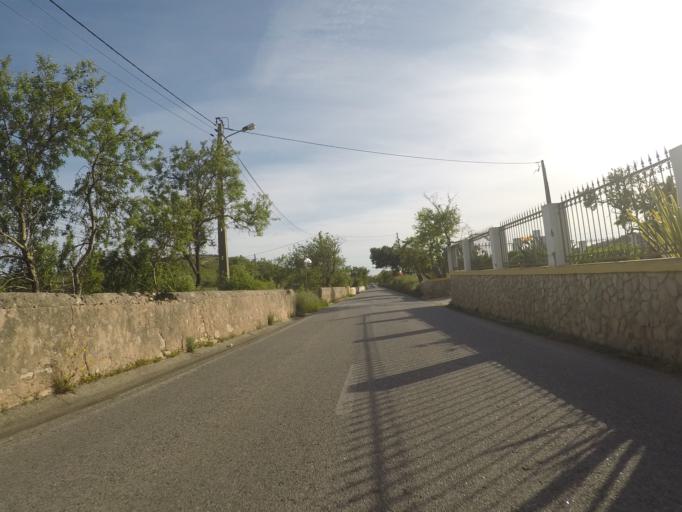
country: PT
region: Faro
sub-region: Lagos
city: Lagos
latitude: 37.1046
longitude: -8.7106
